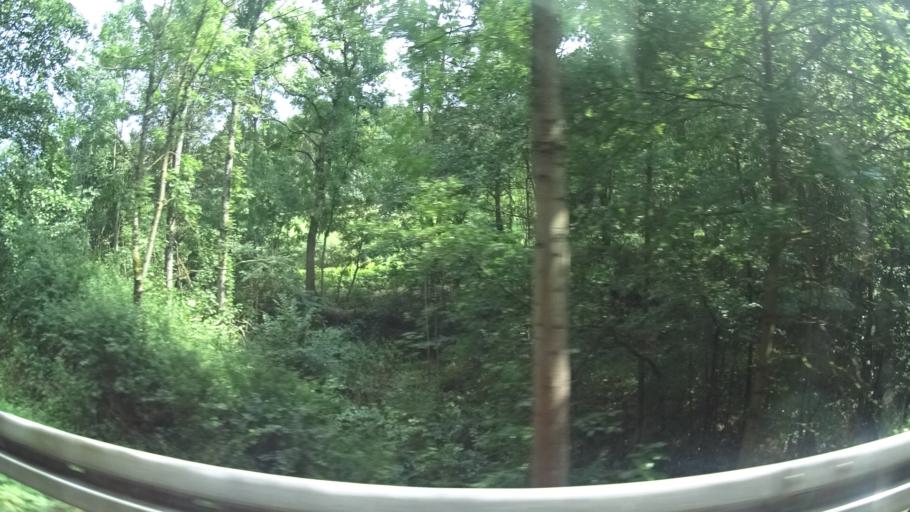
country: DE
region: Hesse
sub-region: Regierungsbezirk Giessen
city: Lauterbach
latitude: 50.6204
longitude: 9.4378
